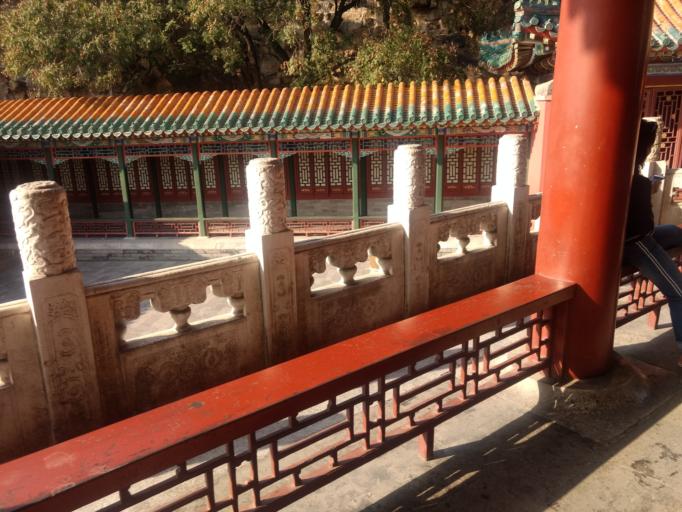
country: CN
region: Beijing
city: Haidian
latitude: 39.9979
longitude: 116.2677
